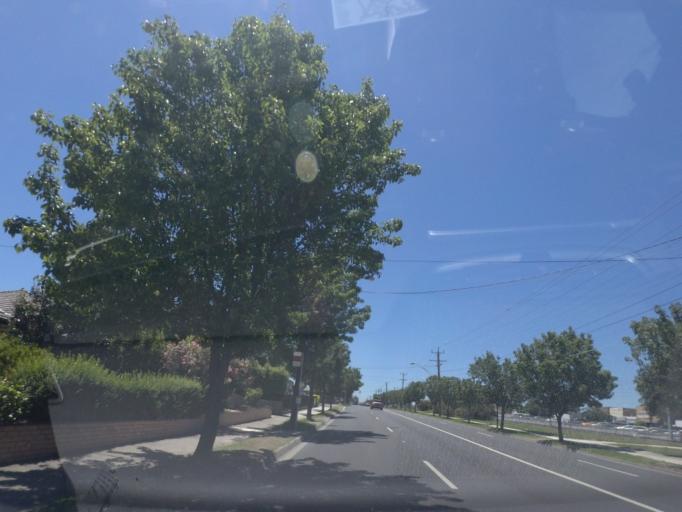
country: AU
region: Victoria
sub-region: Whittlesea
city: Lalor
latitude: -37.6744
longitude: 145.0149
